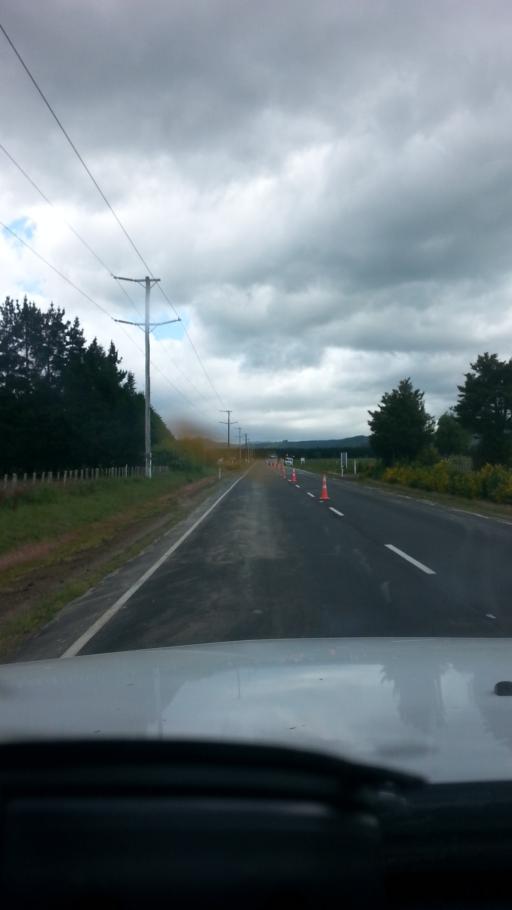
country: NZ
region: Wellington
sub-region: Masterton District
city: Masterton
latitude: -40.8220
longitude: 175.6242
